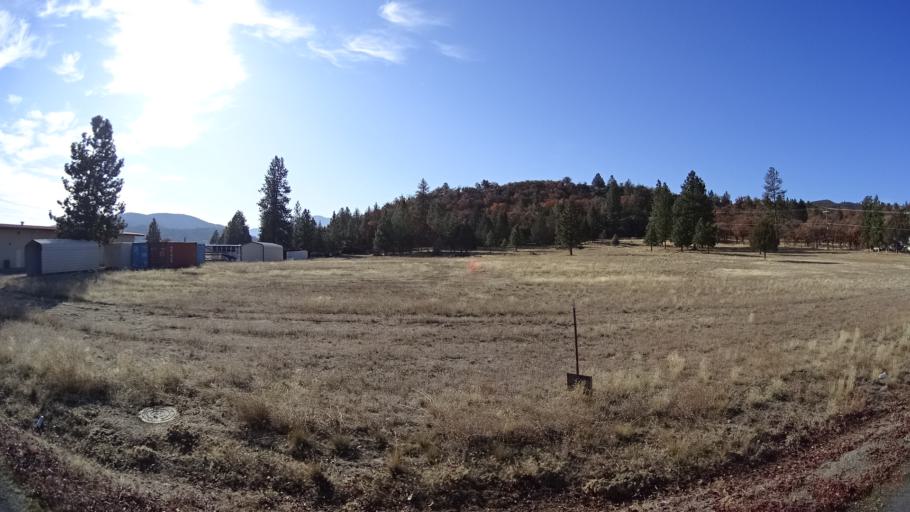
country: US
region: California
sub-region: Siskiyou County
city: Yreka
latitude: 41.7159
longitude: -122.6448
